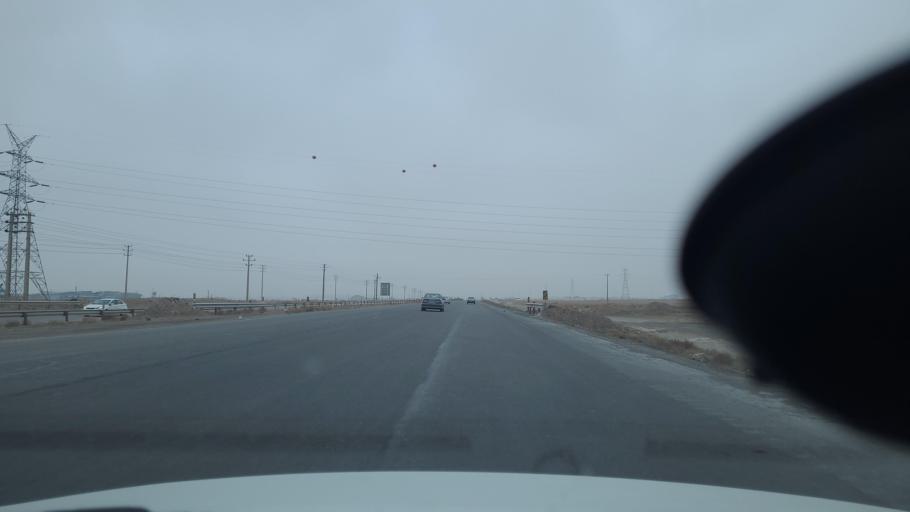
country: IR
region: Razavi Khorasan
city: Fariman
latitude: 35.9417
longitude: 59.7503
